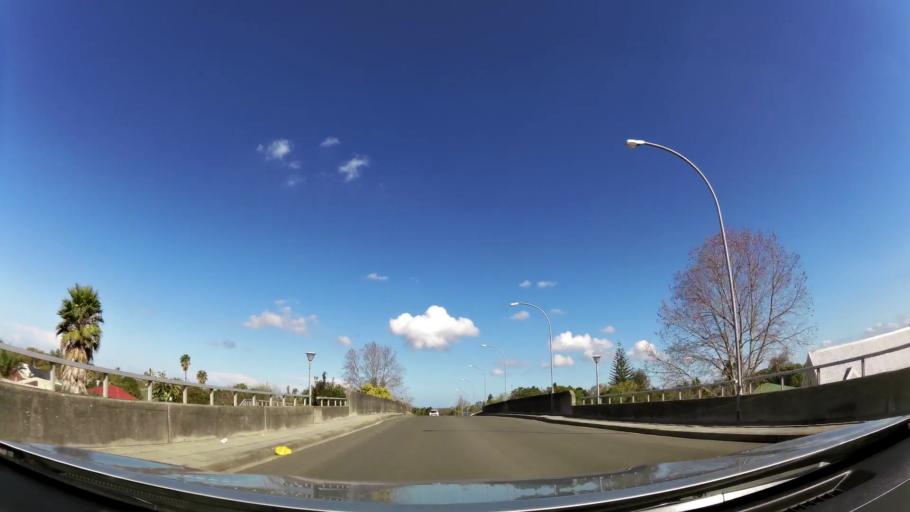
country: ZA
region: Western Cape
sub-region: Eden District Municipality
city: George
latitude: -33.9502
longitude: 22.4659
